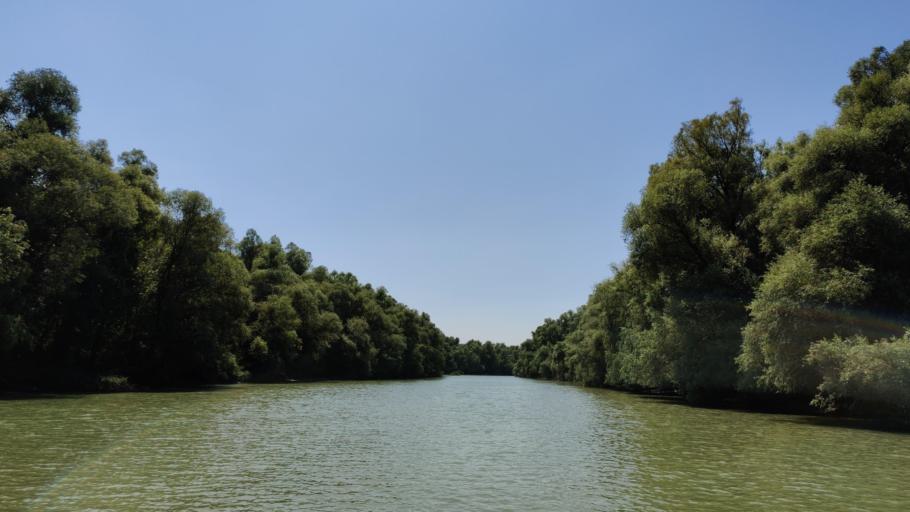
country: RO
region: Tulcea
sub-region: Comuna Pardina
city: Pardina
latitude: 45.2398
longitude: 28.9189
